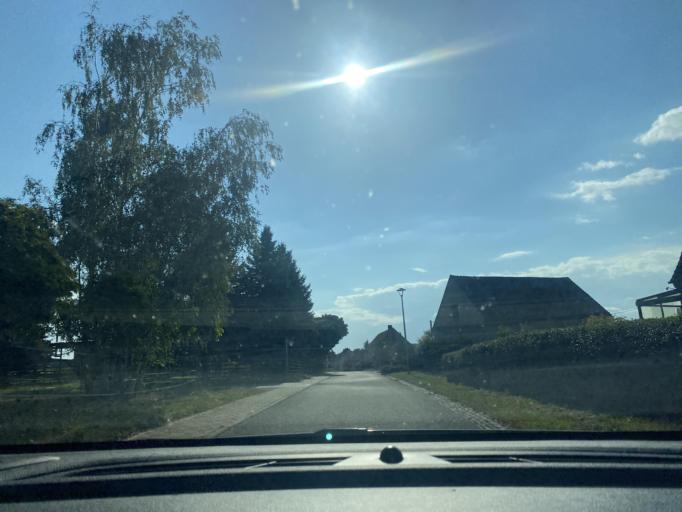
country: DE
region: Saxony
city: Quitzdorf
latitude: 51.2717
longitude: 14.7350
